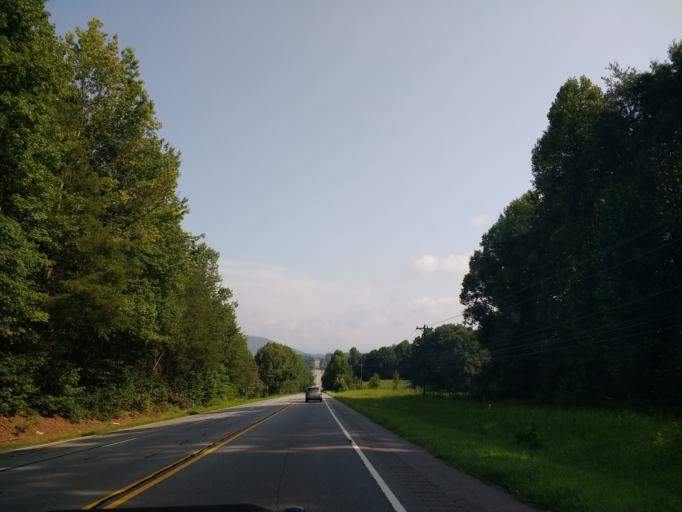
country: US
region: Georgia
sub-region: White County
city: Cleveland
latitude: 34.5271
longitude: -83.7551
